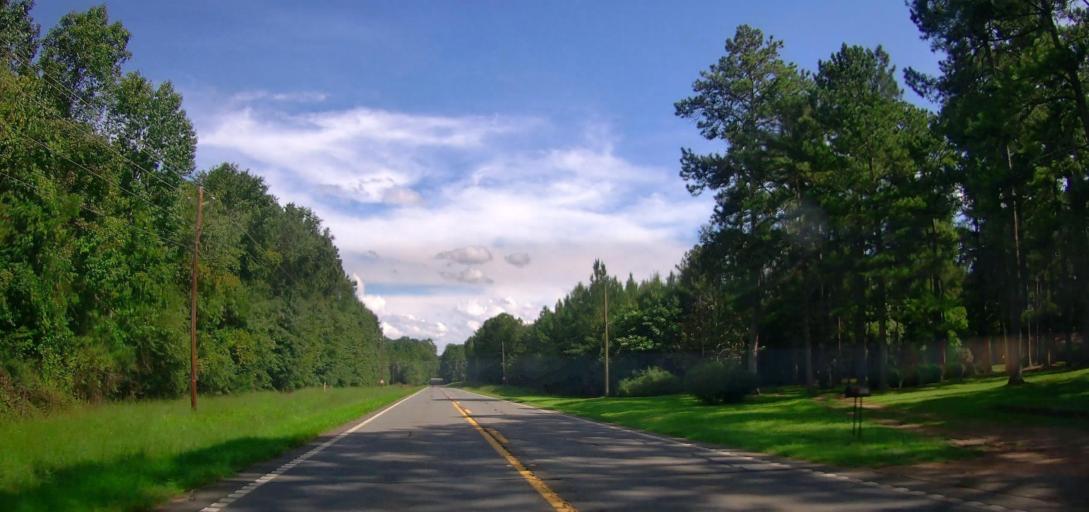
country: US
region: Georgia
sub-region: Talbot County
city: Sardis
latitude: 32.8223
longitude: -84.6122
